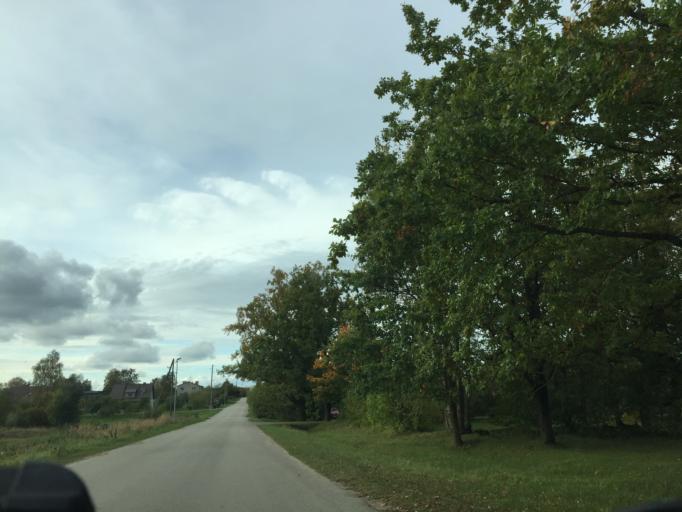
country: LV
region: Auces Novads
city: Auce
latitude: 56.5429
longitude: 22.9939
